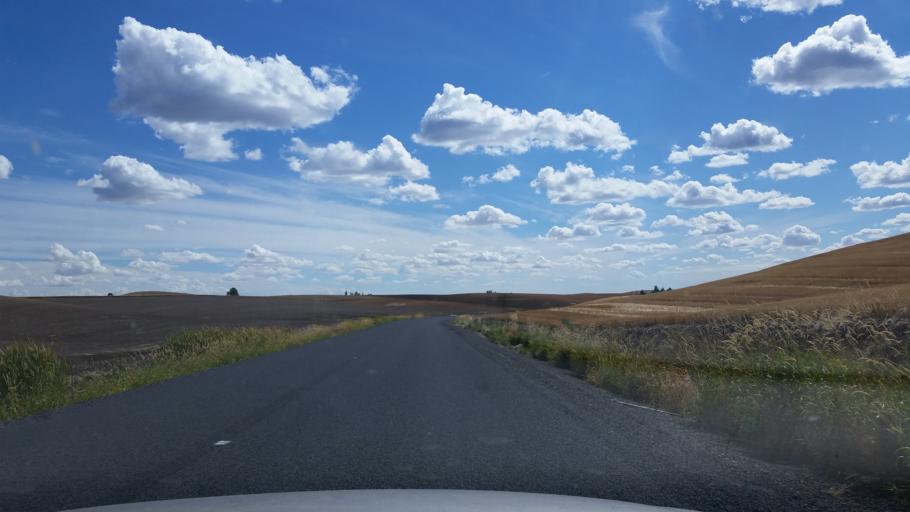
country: US
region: Washington
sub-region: Spokane County
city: Cheney
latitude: 47.4988
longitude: -117.6214
